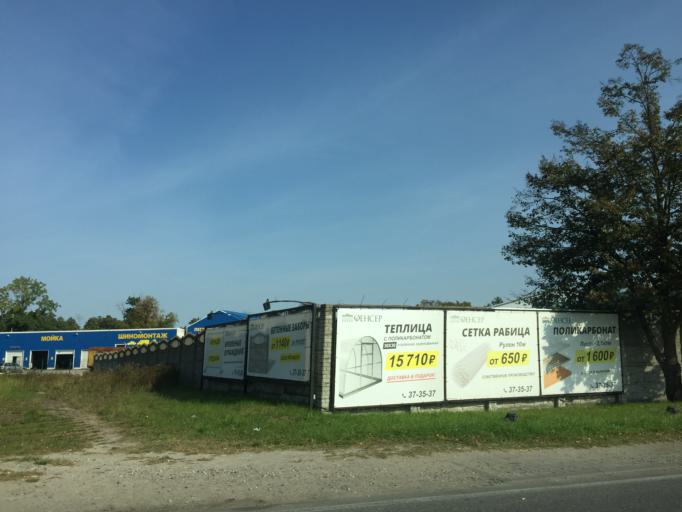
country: RU
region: Kaliningrad
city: Bol'shoe Isakovo
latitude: 54.6811
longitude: 20.5896
